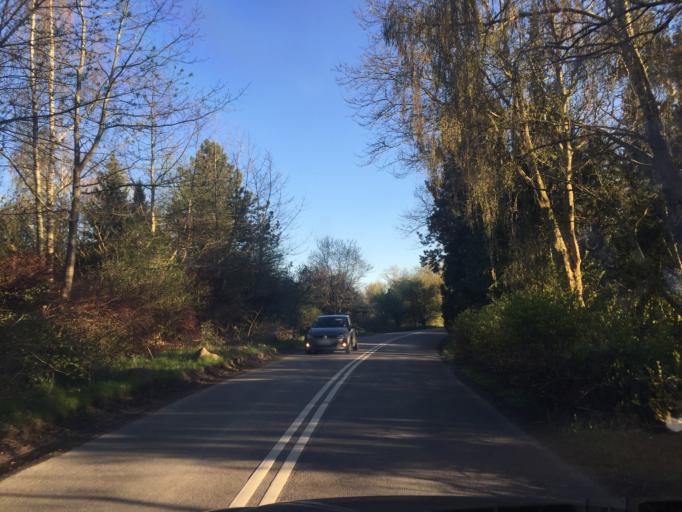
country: DK
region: Capital Region
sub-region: Egedal Kommune
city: Smorumnedre
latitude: 55.7104
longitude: 12.2664
